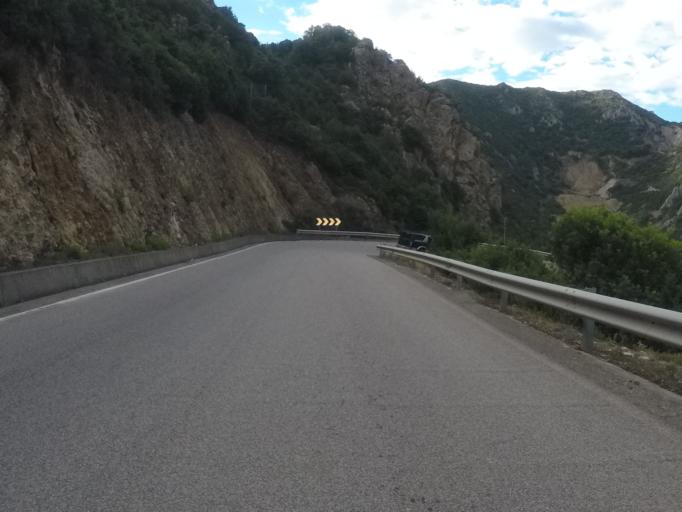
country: IT
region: Sardinia
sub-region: Provincia di Carbonia-Iglesias
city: Buggerru
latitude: 39.3357
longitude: 8.4409
